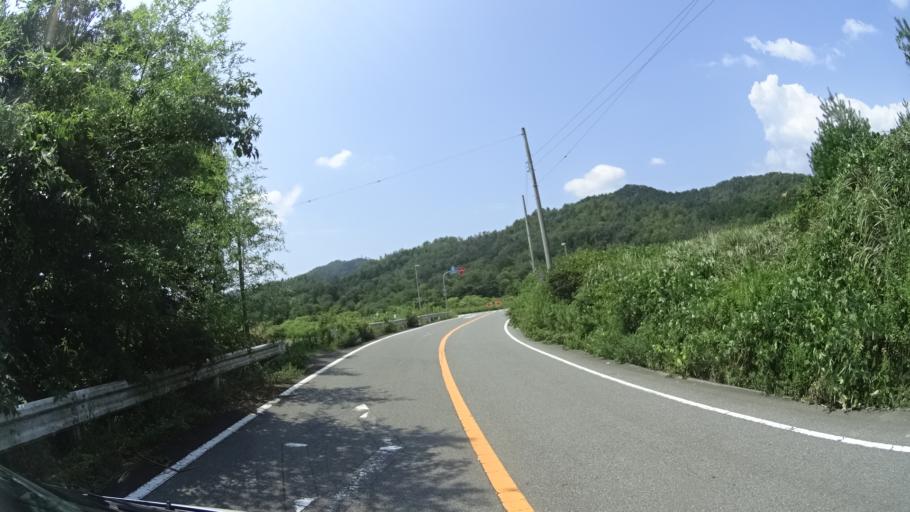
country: JP
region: Kyoto
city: Fukuchiyama
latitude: 35.2574
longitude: 135.1466
